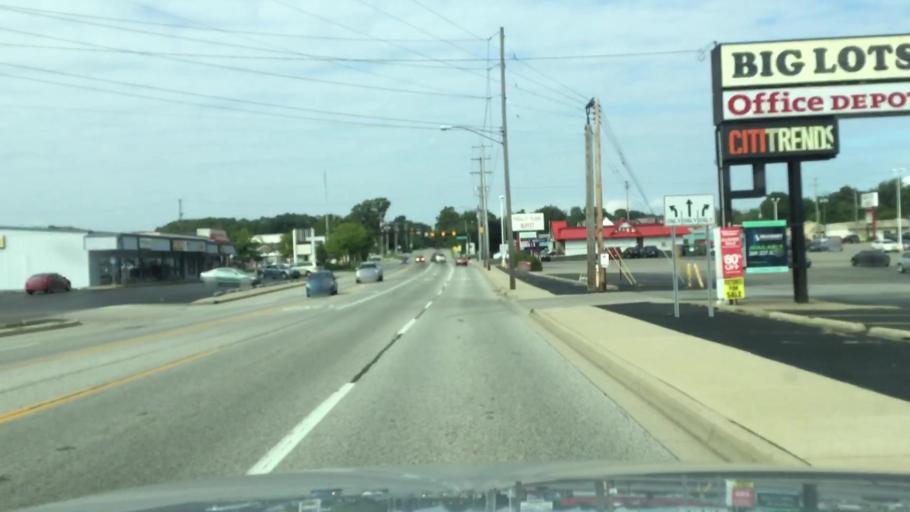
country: US
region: Michigan
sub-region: Kalamazoo County
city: Portage
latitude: 42.2456
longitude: -85.5877
